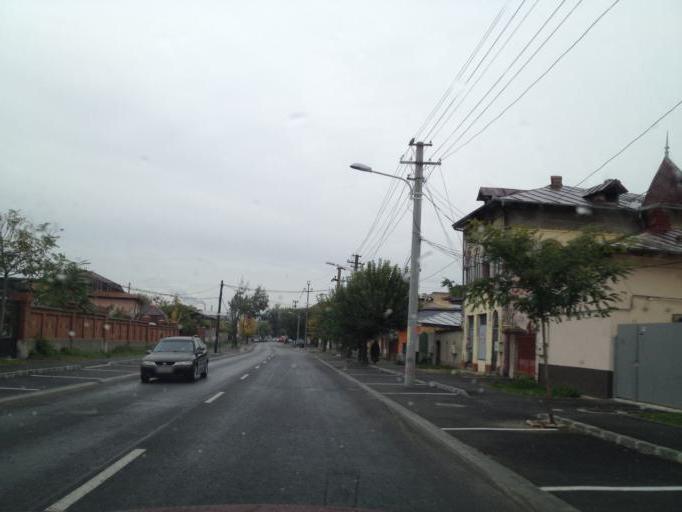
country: RO
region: Dolj
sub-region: Municipiul Craiova
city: Mofleni
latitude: 44.3139
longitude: 23.7743
